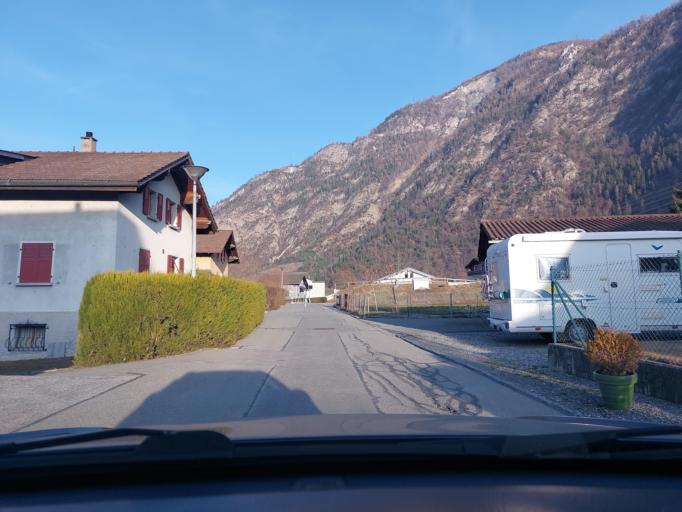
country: CH
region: Valais
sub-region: Martigny District
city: Riddes
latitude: 46.1742
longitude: 7.2262
